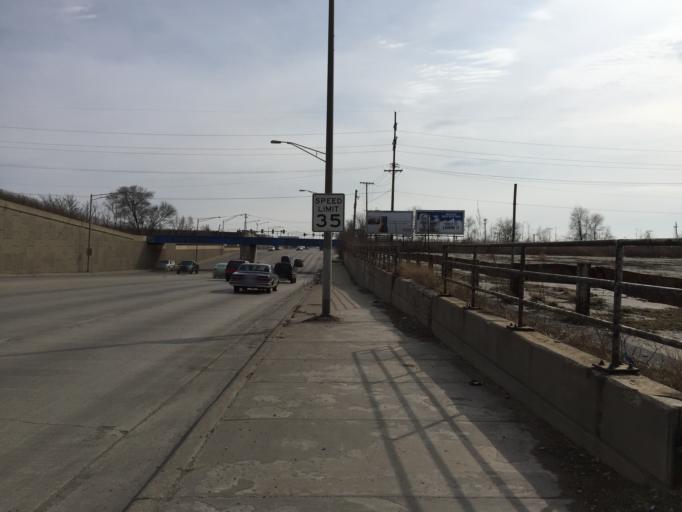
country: US
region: Illinois
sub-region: Cook County
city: Cicero
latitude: 41.8338
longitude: -87.7439
